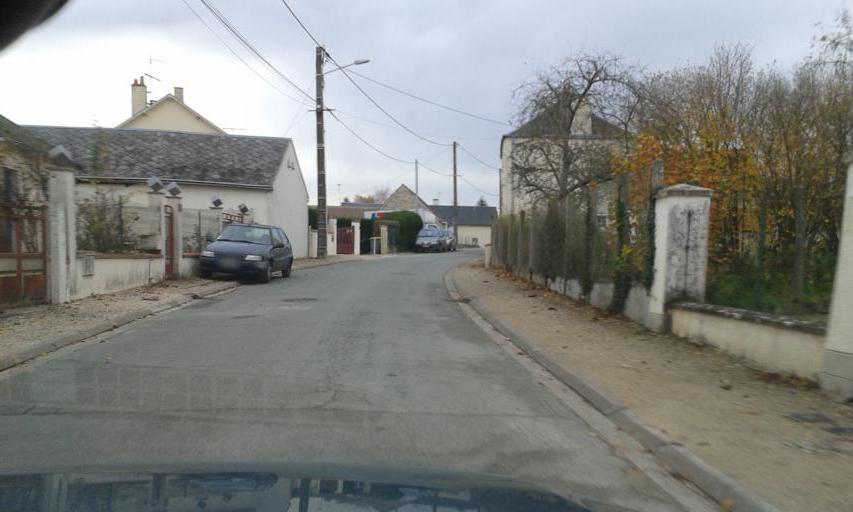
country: FR
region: Centre
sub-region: Departement du Loiret
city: Gidy
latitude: 47.9832
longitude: 1.8332
